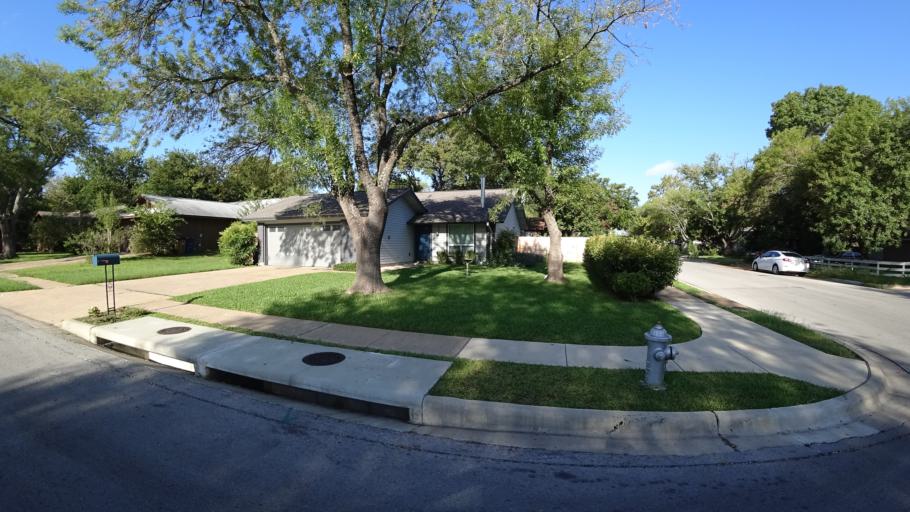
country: US
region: Texas
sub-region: Travis County
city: Shady Hollow
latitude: 30.2086
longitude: -97.8086
